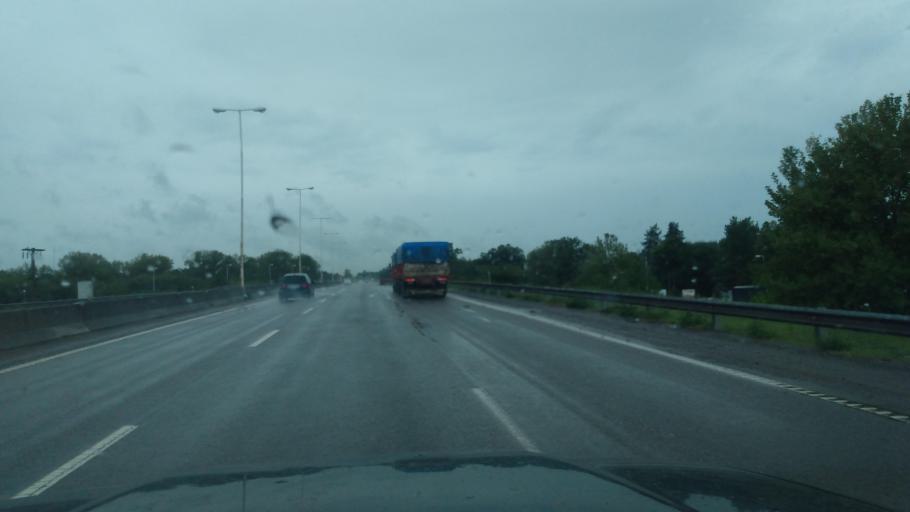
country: AR
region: Buenos Aires
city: Capilla del Senor
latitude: -34.3913
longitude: -59.0360
